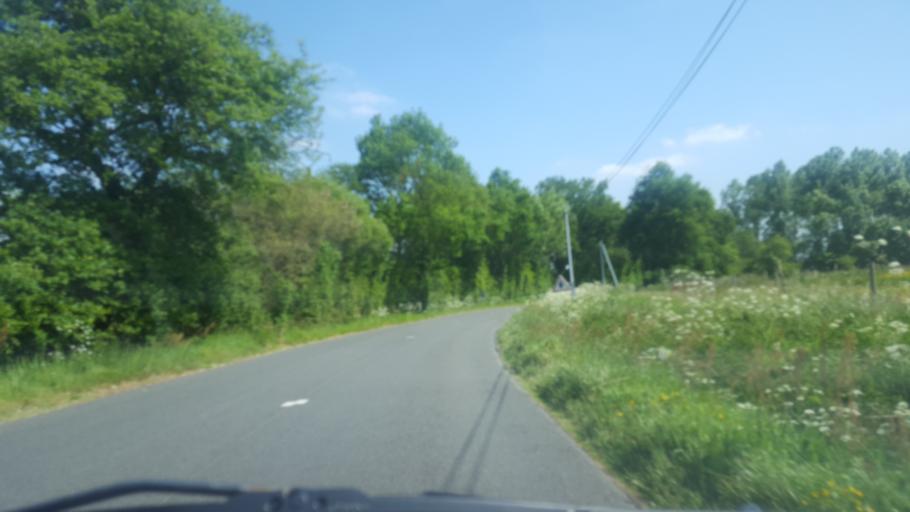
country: FR
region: Pays de la Loire
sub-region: Departement de la Loire-Atlantique
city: La Limouziniere
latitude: 47.0362
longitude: -1.5818
